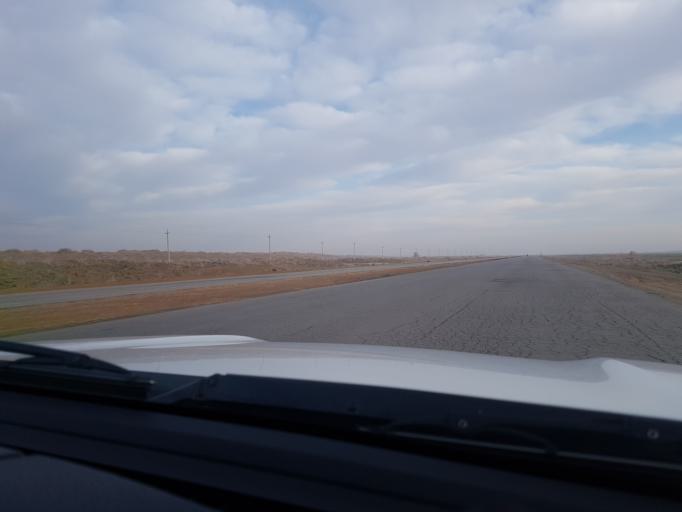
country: TM
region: Ahal
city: Abadan
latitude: 38.6000
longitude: 58.5014
